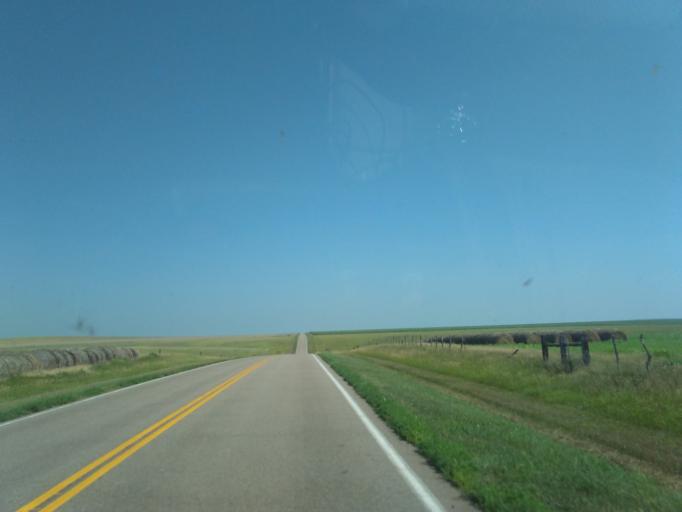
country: US
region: Nebraska
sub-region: Dundy County
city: Benkelman
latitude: 39.9098
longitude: -101.5412
